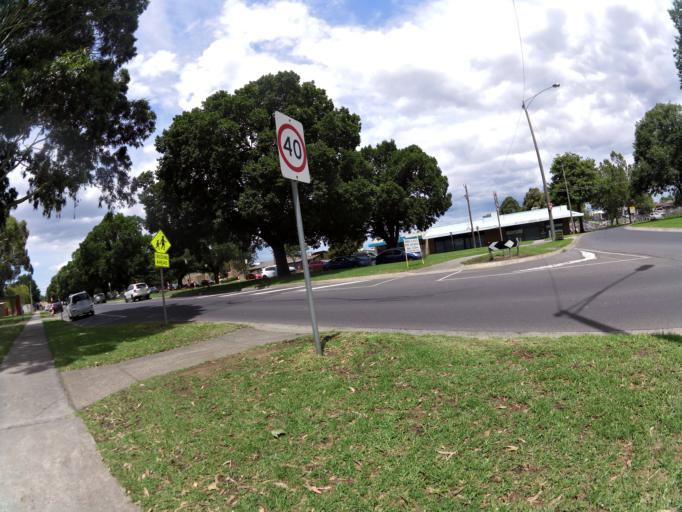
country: AU
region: Victoria
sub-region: Latrobe
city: Traralgon
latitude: -38.1939
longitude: 146.5337
